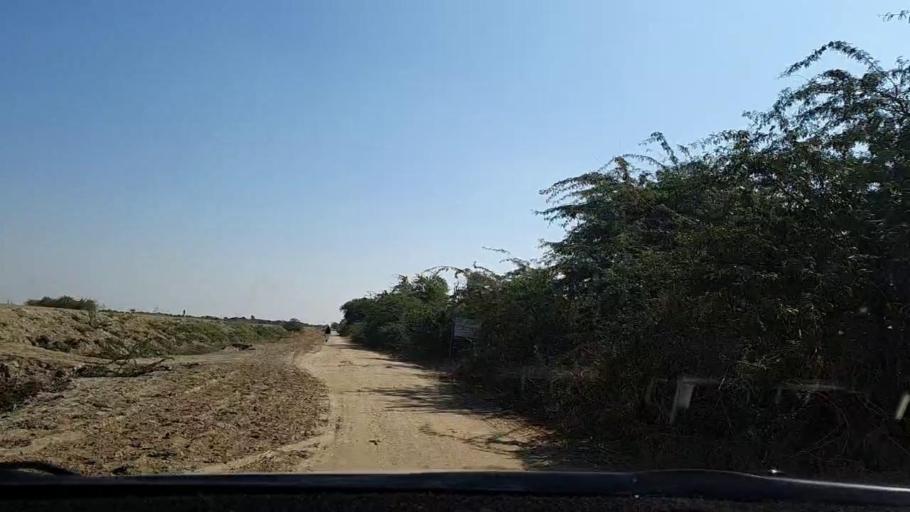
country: PK
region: Sindh
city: Tando Mittha Khan
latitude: 25.7677
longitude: 69.3015
